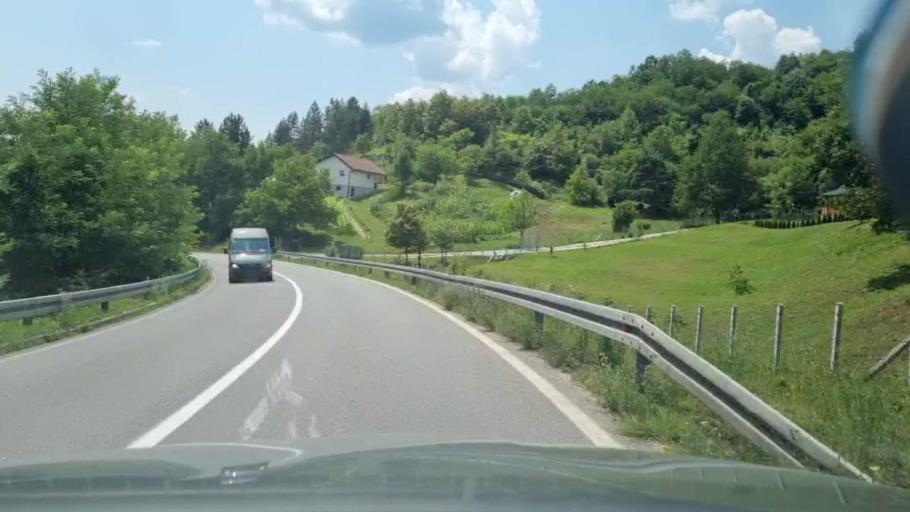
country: BA
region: Federation of Bosnia and Herzegovina
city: Gornja Tuzla
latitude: 44.5394
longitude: 18.7926
